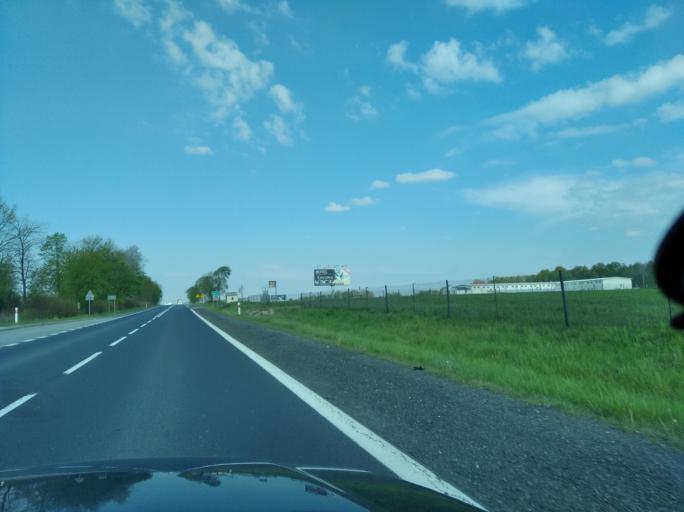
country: PL
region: Subcarpathian Voivodeship
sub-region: Powiat lubaczowski
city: Wielkie Oczy
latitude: 49.9684
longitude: 23.0606
